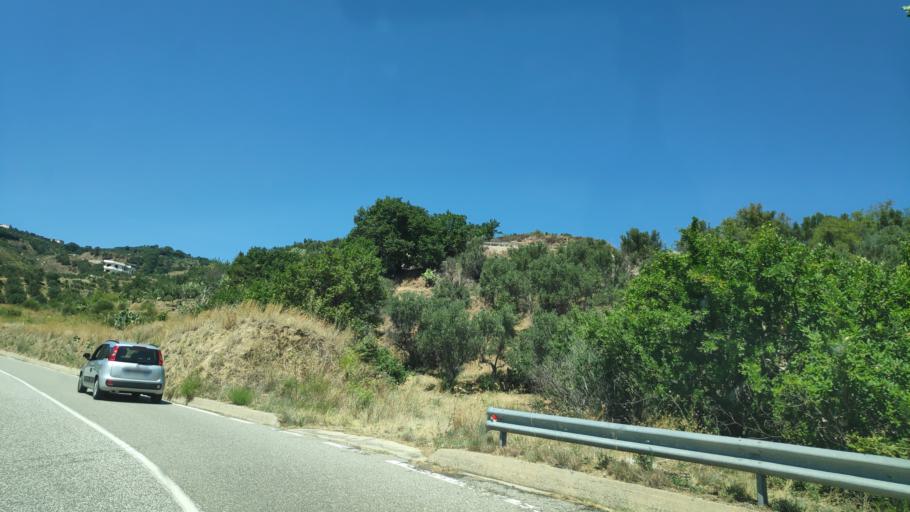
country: IT
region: Calabria
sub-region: Provincia di Catanzaro
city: Montauro
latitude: 38.7457
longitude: 16.5213
